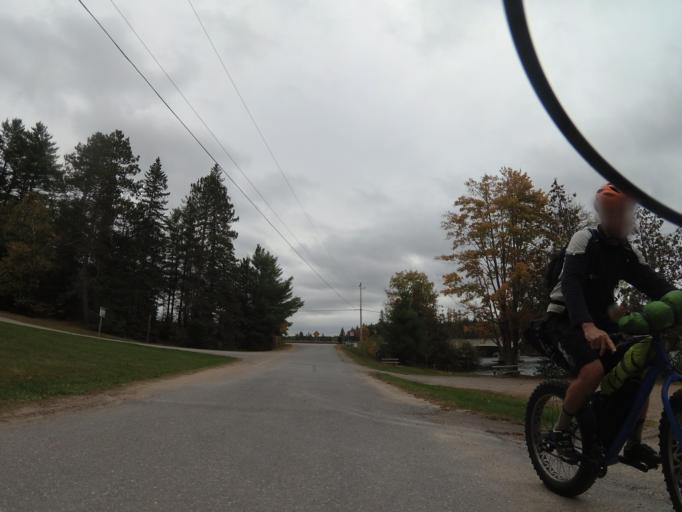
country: CA
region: Ontario
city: Renfrew
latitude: 45.2508
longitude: -77.1864
